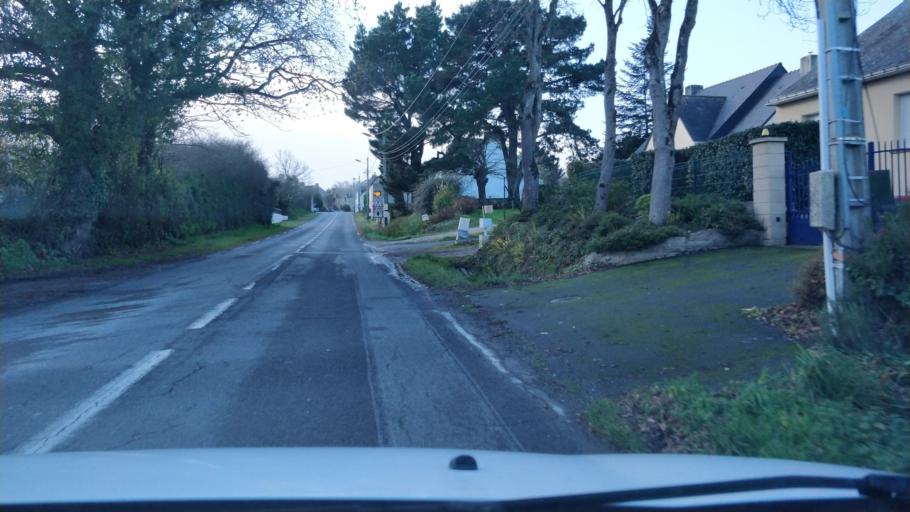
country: FR
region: Pays de la Loire
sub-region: Departement de la Loire-Atlantique
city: Asserac
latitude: 47.4176
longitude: -2.3997
